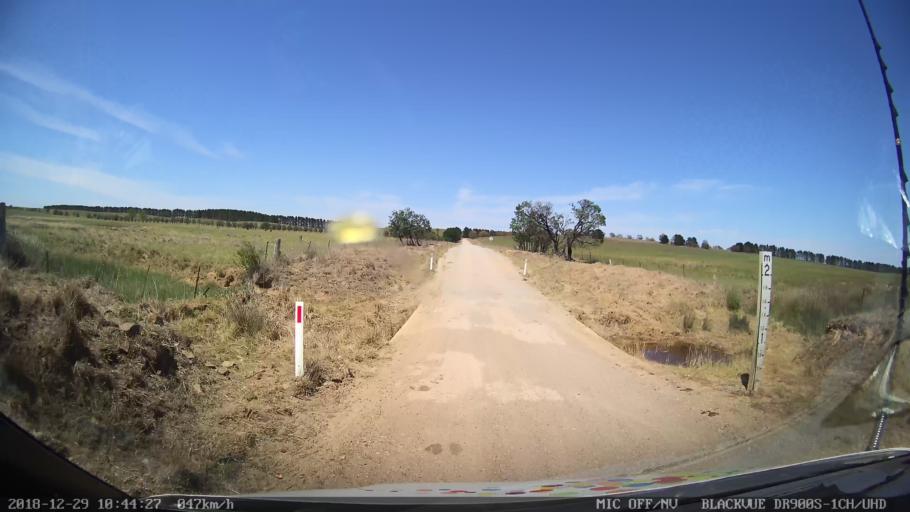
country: AU
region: New South Wales
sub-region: Palerang
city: Bungendore
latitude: -35.0417
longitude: 149.5287
